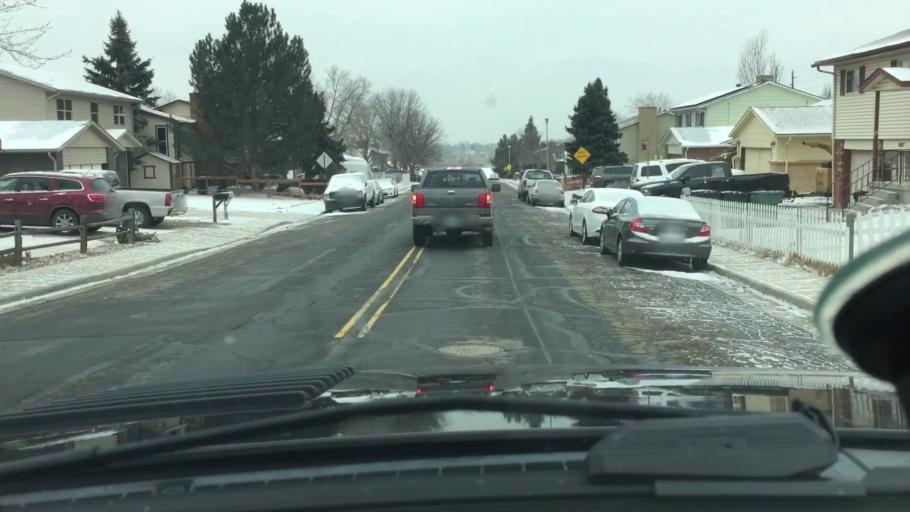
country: US
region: Colorado
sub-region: Adams County
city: Northglenn
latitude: 39.8742
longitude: -105.0056
